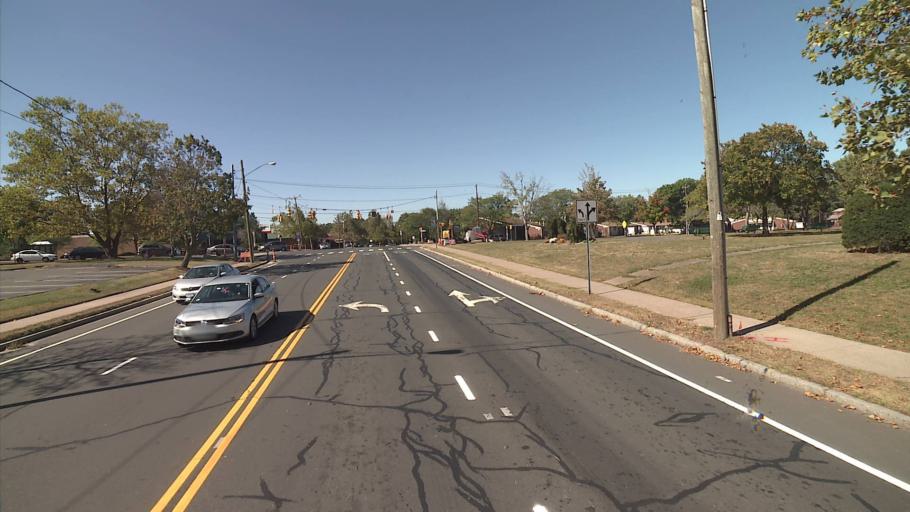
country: US
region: Connecticut
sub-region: Hartford County
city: Manchester
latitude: 41.7951
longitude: -72.5245
